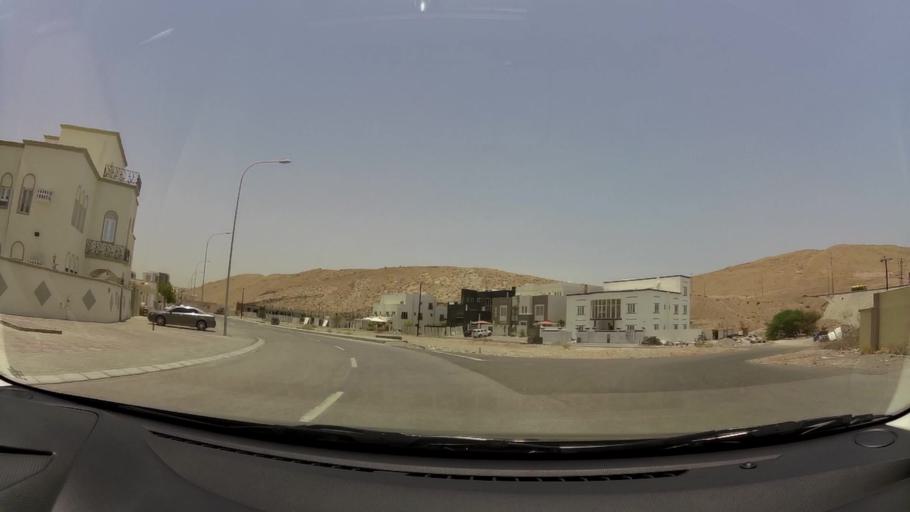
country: OM
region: Muhafazat Masqat
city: Bawshar
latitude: 23.5691
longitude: 58.4239
